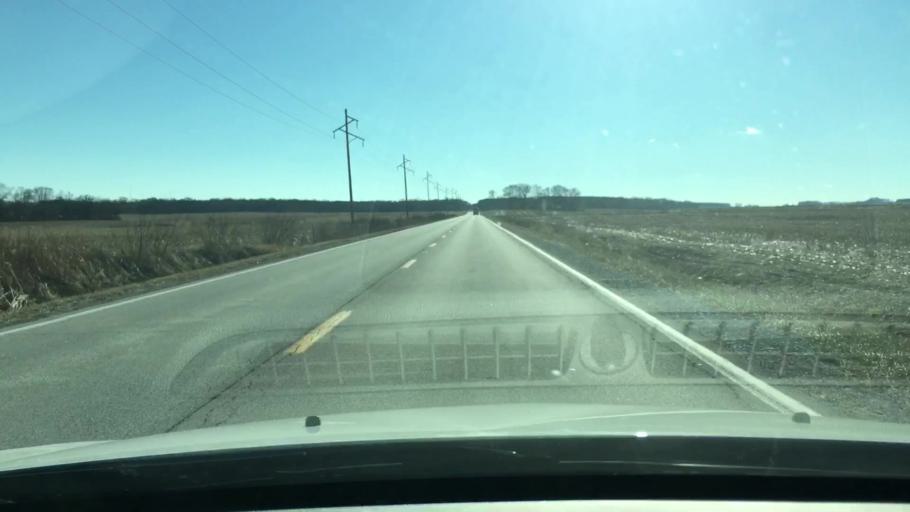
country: US
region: Illinois
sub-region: Morgan County
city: Meredosia
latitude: 39.9225
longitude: -90.4945
